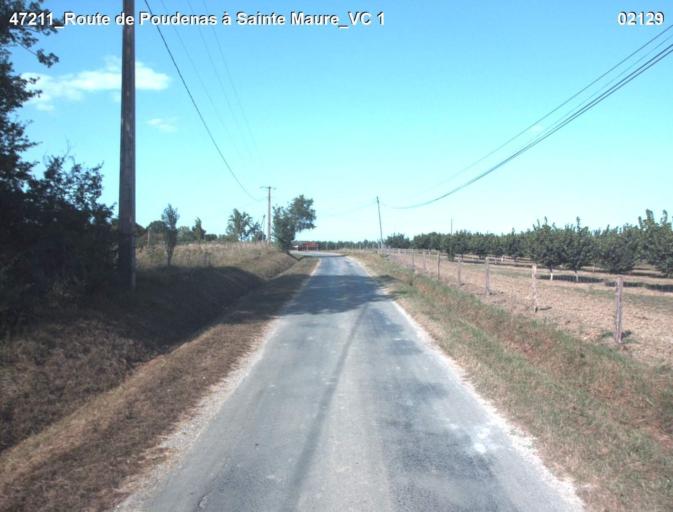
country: FR
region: Aquitaine
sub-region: Departement du Lot-et-Garonne
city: Mezin
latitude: 44.0313
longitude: 0.2045
